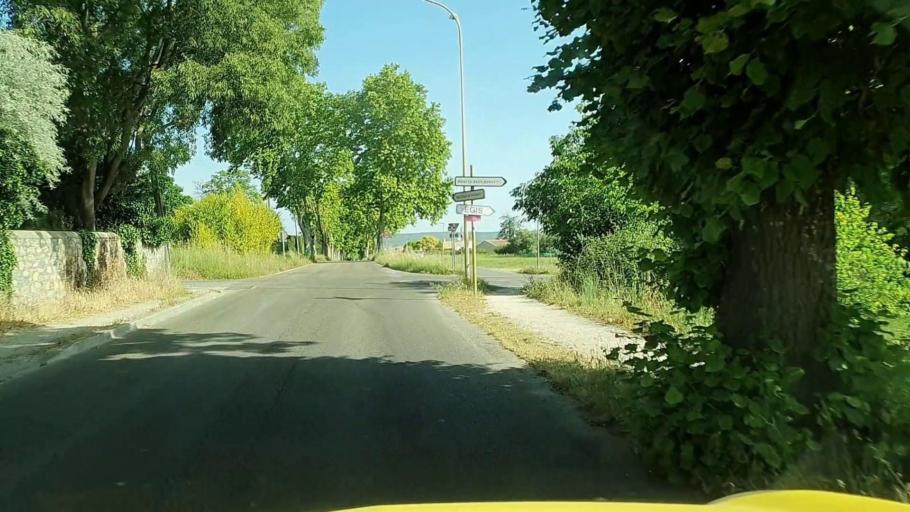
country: FR
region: Languedoc-Roussillon
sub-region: Departement du Gard
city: Uzes
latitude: 44.0209
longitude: 4.4150
